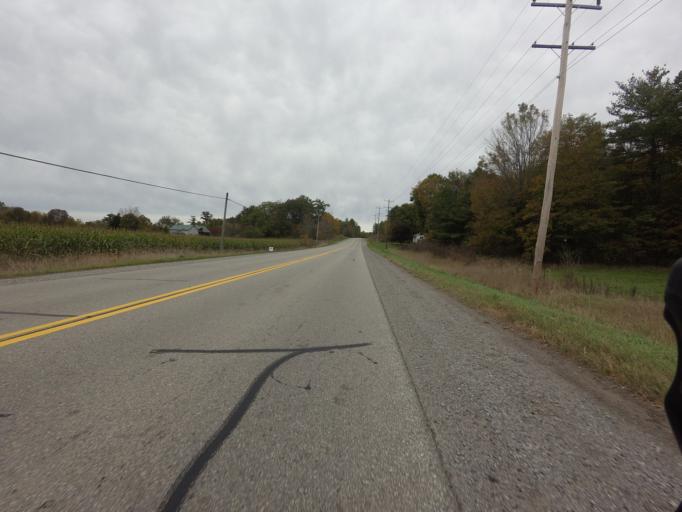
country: CA
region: Ontario
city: Gananoque
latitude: 44.5679
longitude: -76.1111
